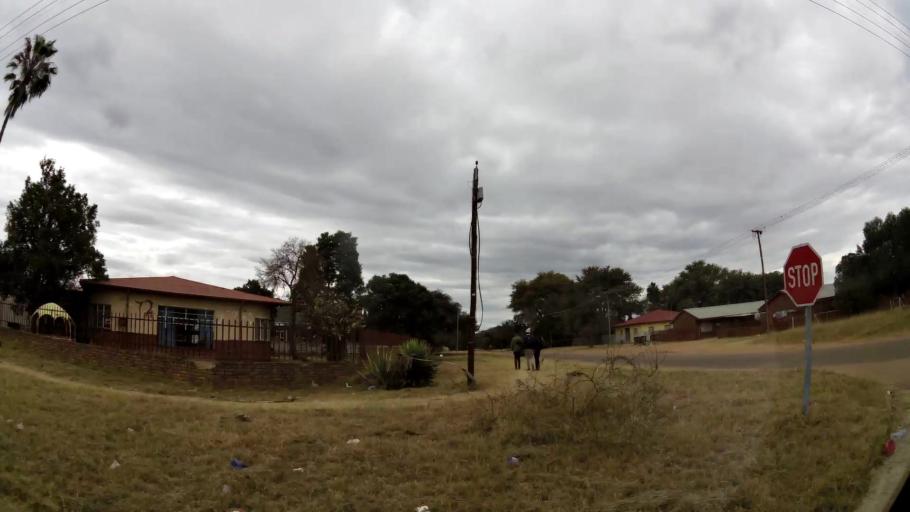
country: ZA
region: Limpopo
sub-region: Waterberg District Municipality
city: Modimolle
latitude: -24.7065
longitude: 28.4146
